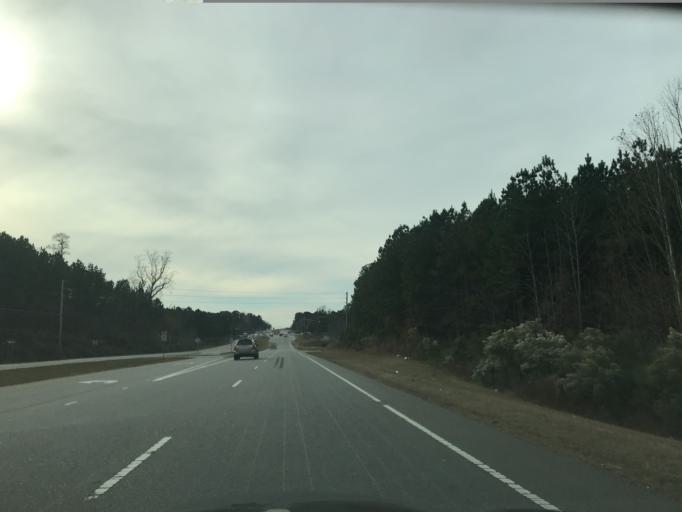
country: US
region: North Carolina
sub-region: Wake County
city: Rolesville
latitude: 35.8981
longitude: -78.5016
